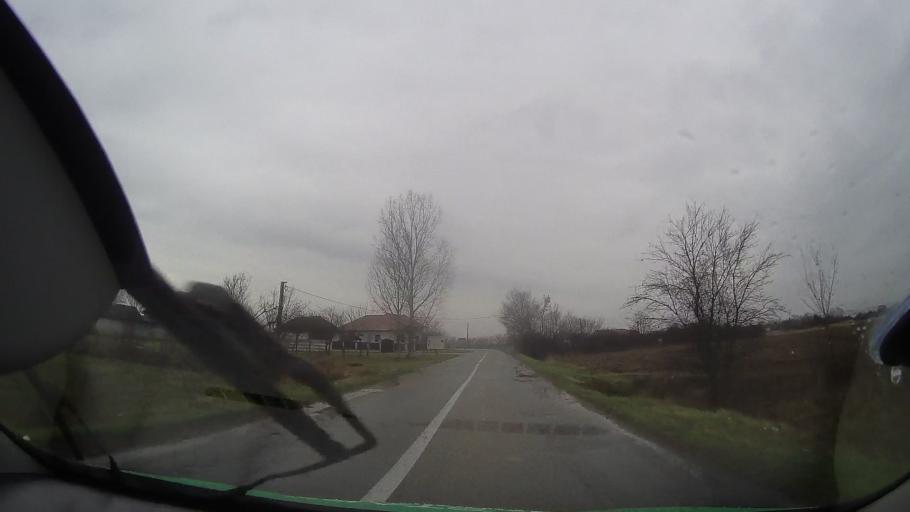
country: RO
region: Bihor
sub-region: Comuna Cociuba Mare
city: Cociuba Mare
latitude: 46.7392
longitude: 21.9876
